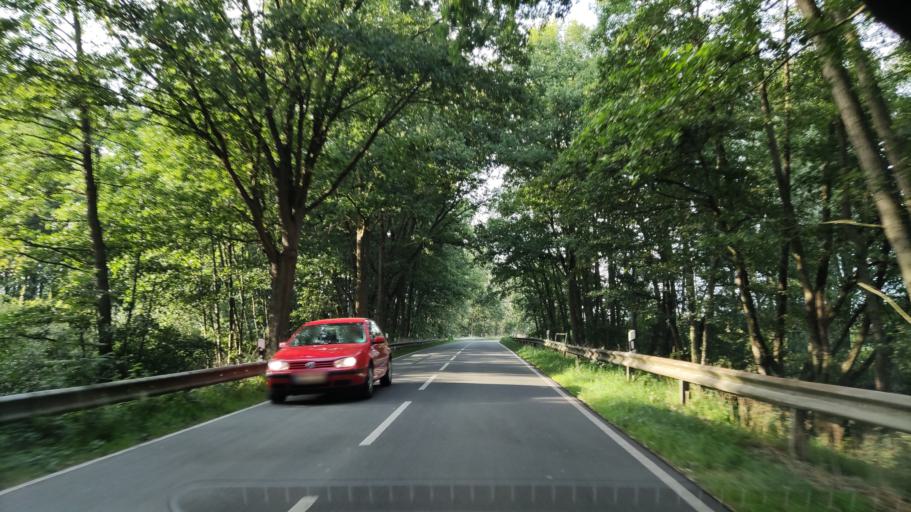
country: DE
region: Lower Saxony
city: Dannenberg
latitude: 53.1137
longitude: 11.1129
